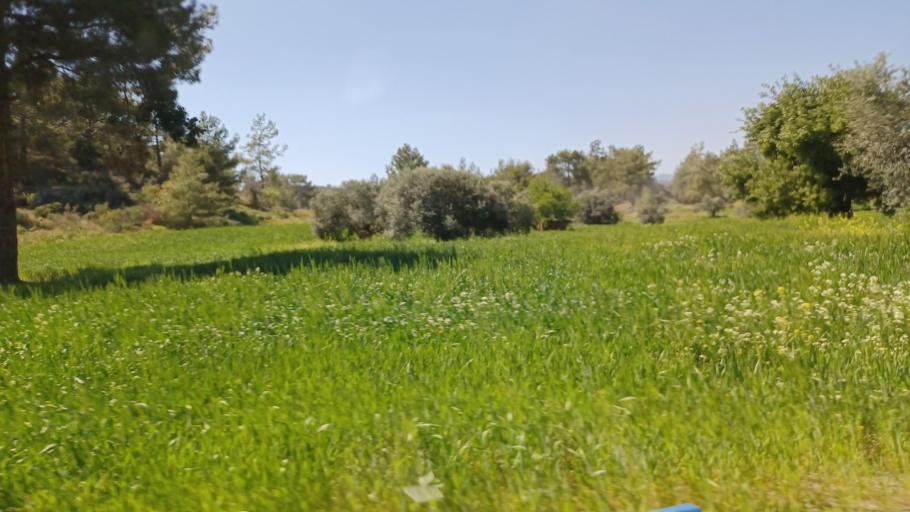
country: CY
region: Limassol
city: Parekklisha
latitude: 34.7993
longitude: 33.1351
